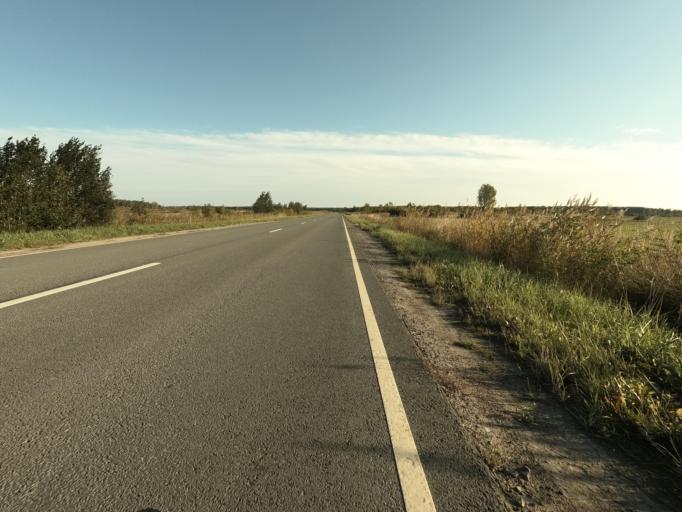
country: RU
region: St.-Petersburg
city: Sapernyy
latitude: 59.7363
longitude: 30.6548
